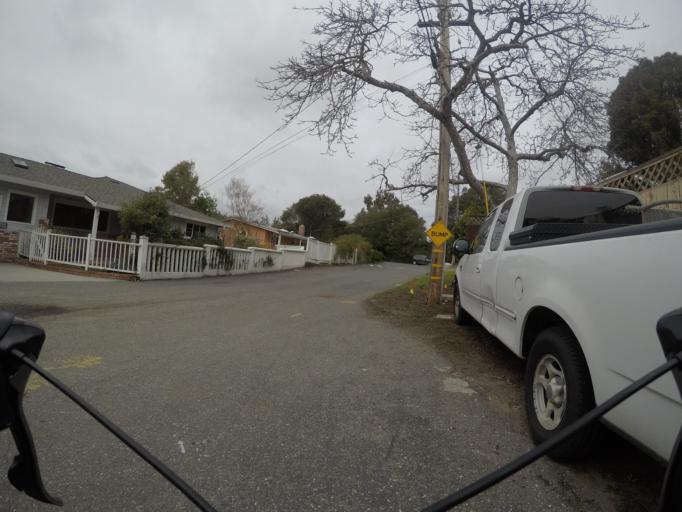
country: US
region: California
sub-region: Santa Cruz County
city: Scotts Valley
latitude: 37.0624
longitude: -122.0011
